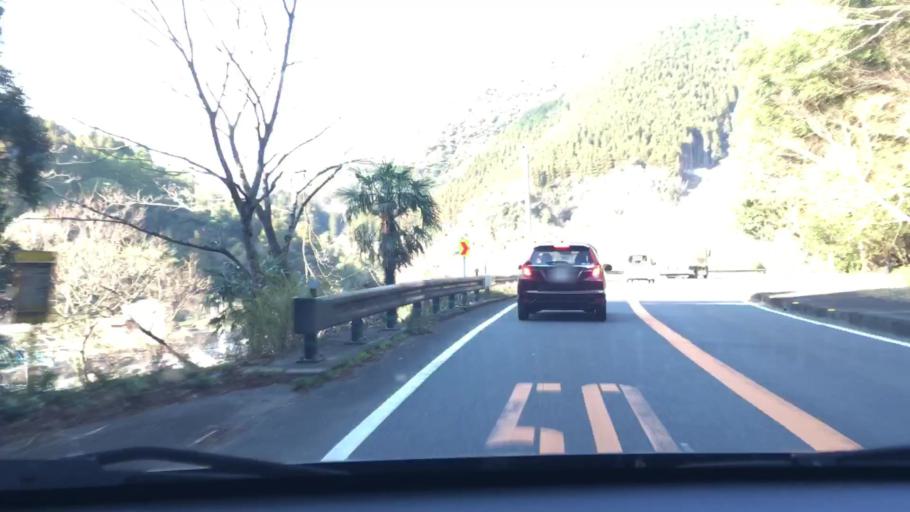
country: JP
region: Oita
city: Saiki
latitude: 32.9925
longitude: 131.8291
